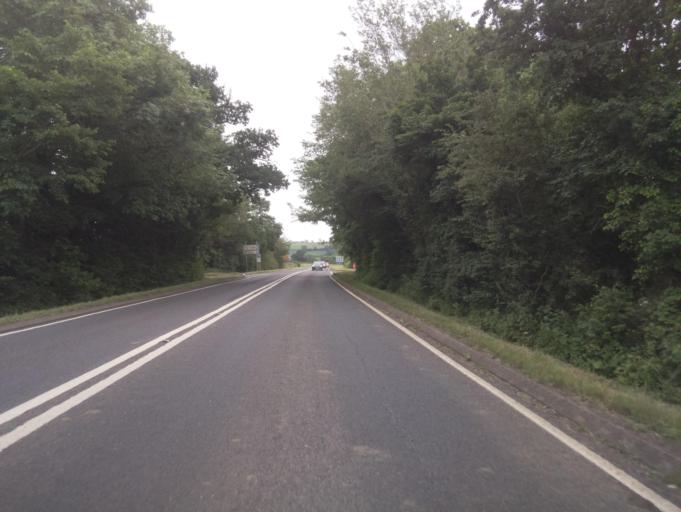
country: GB
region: England
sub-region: Leicestershire
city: Melton Mowbray
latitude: 52.7180
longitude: -0.8301
